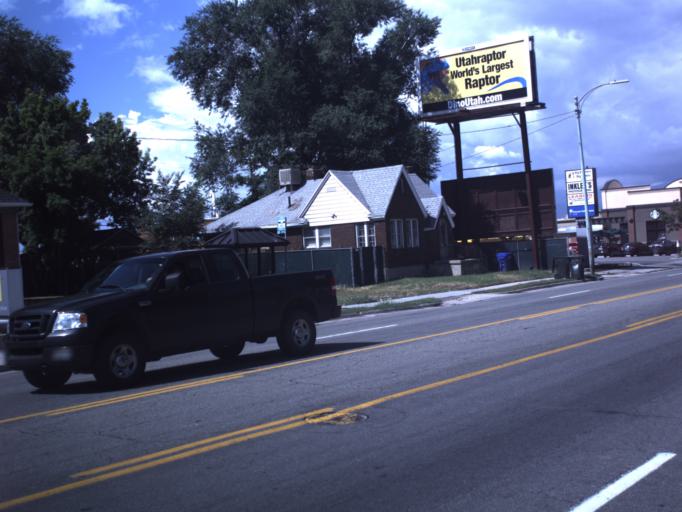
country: US
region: Utah
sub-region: Salt Lake County
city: South Salt Lake
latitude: 40.7255
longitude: -111.8867
